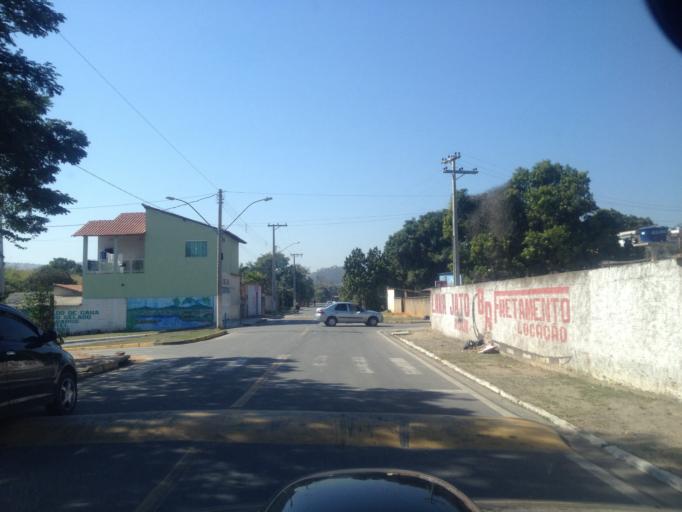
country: BR
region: Rio de Janeiro
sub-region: Porto Real
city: Porto Real
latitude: -22.4487
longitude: -44.3085
